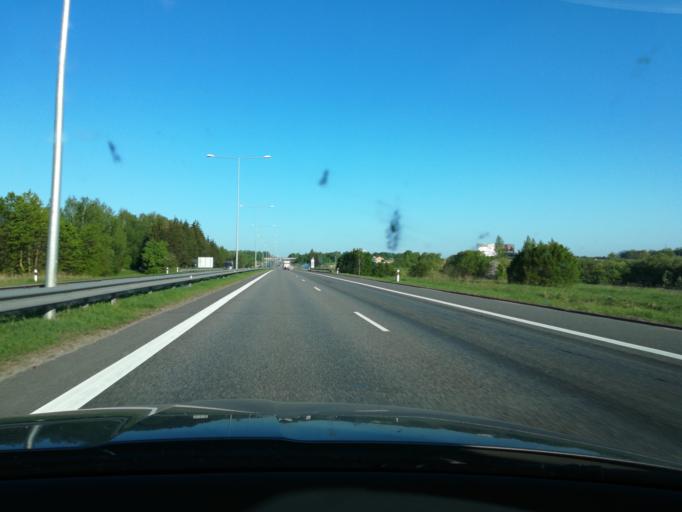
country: LT
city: Ziezmariai
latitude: 54.8146
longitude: 24.4428
